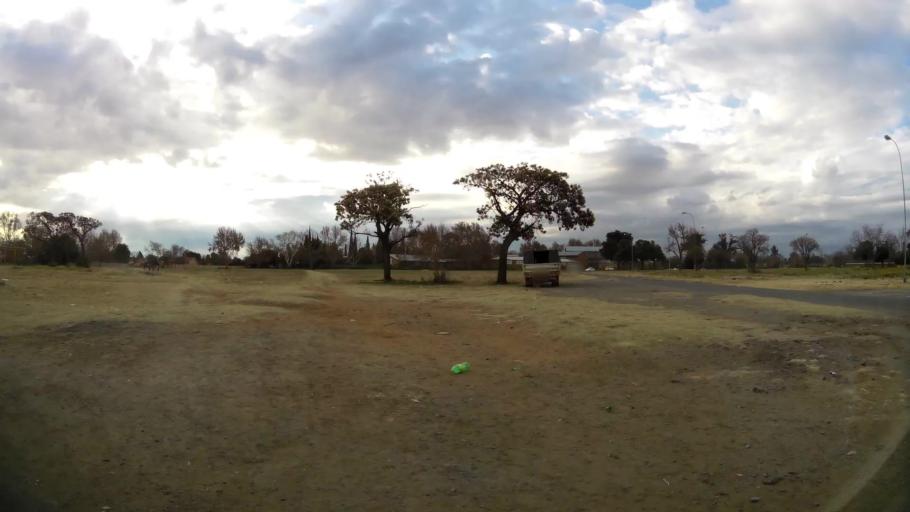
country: ZA
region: Orange Free State
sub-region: Lejweleputswa District Municipality
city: Welkom
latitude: -27.9896
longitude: 26.7111
